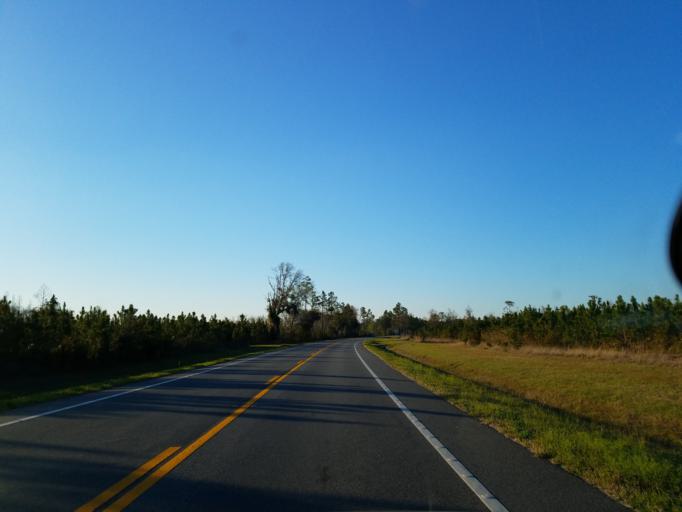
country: US
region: Georgia
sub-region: Echols County
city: Statenville
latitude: 30.6108
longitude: -83.0216
